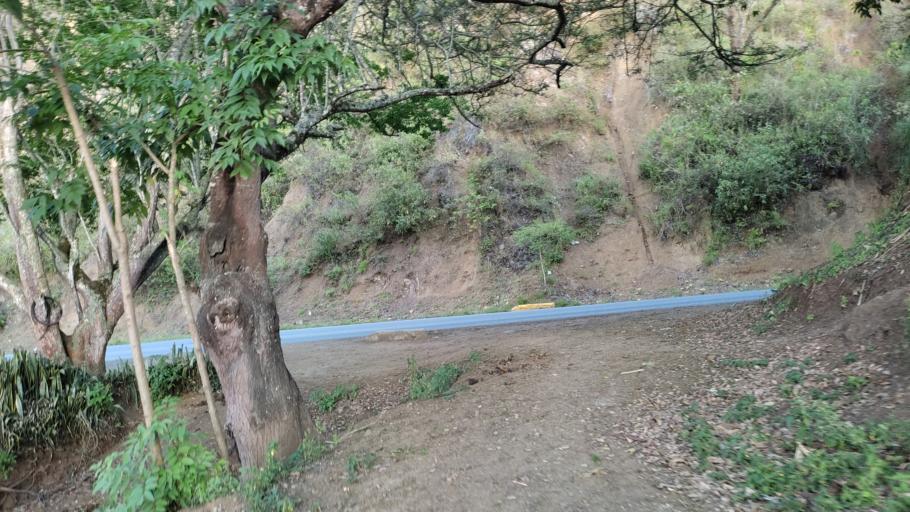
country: CO
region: Narino
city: Taminango
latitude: 1.5419
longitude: -77.3673
